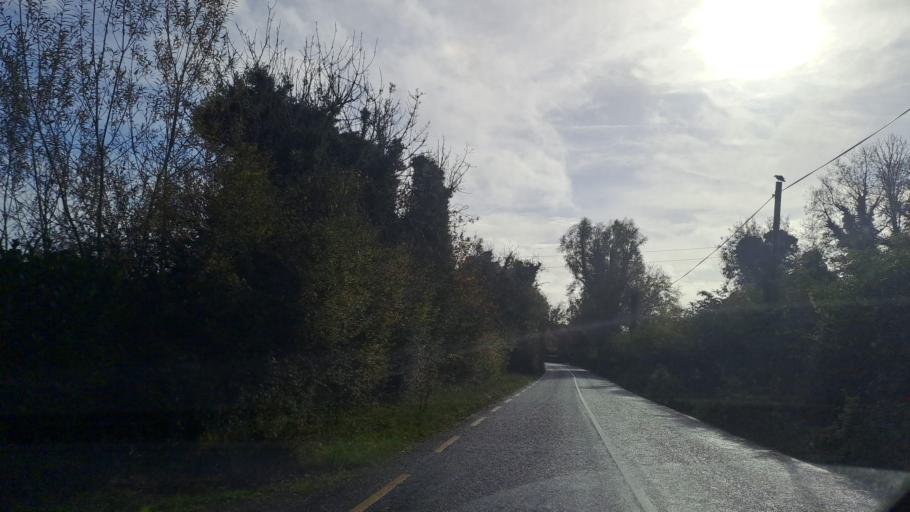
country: IE
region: Ulster
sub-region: County Monaghan
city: Carrickmacross
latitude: 53.9146
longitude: -6.7081
